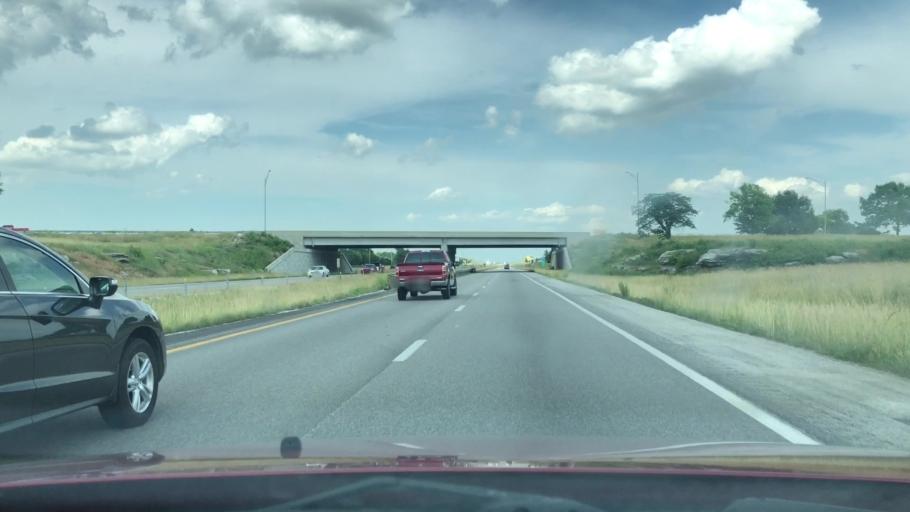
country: US
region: Missouri
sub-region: Greene County
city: Springfield
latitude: 37.2500
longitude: -93.2644
